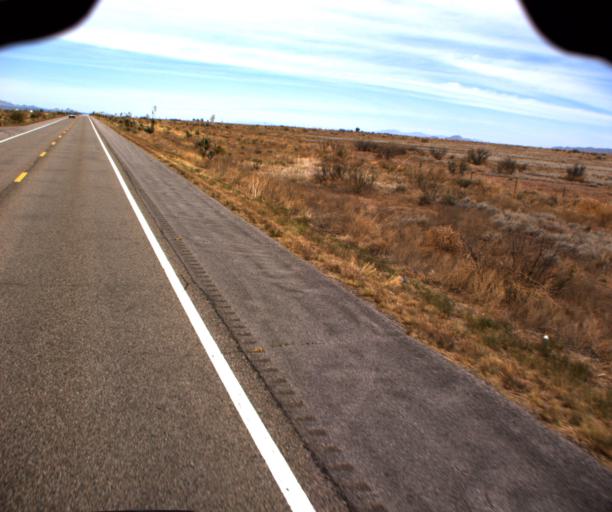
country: US
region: Arizona
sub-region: Cochise County
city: Pirtleville
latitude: 31.5356
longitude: -109.6541
